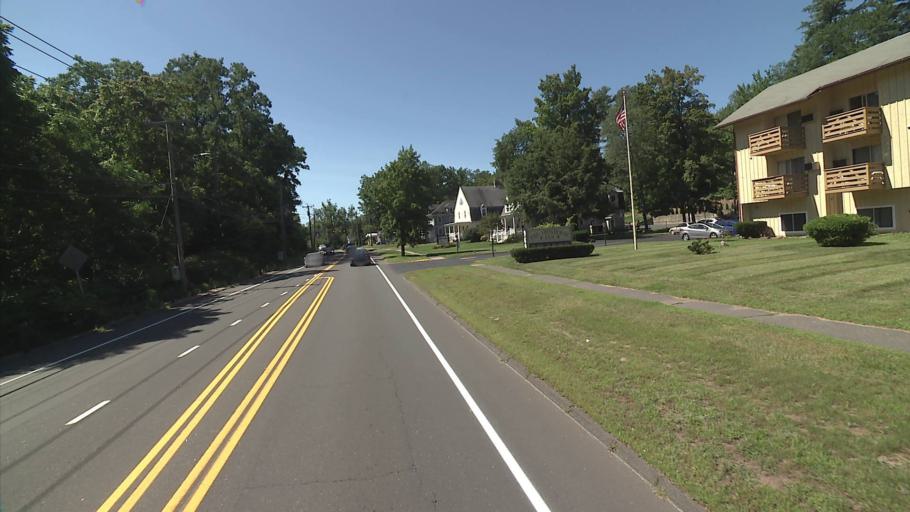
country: US
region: Connecticut
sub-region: Hartford County
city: Simsbury Center
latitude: 41.8840
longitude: -72.7994
